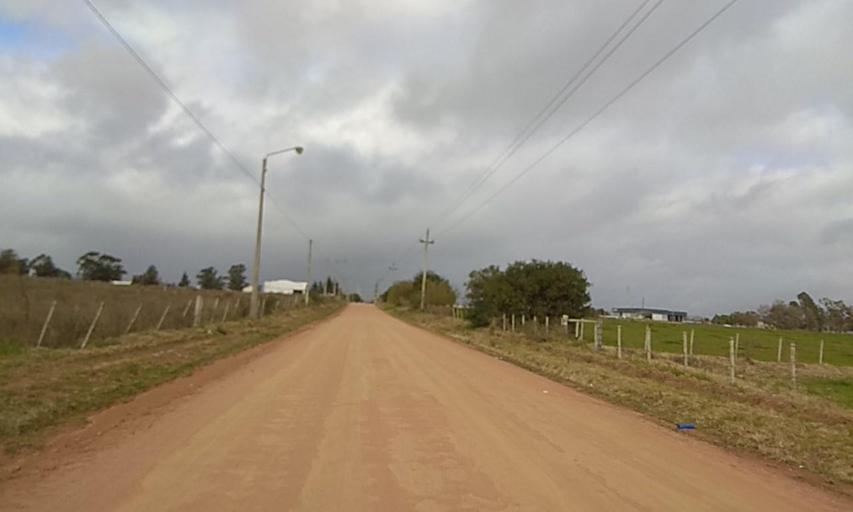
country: UY
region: Florida
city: Florida
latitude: -34.0749
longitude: -56.2218
